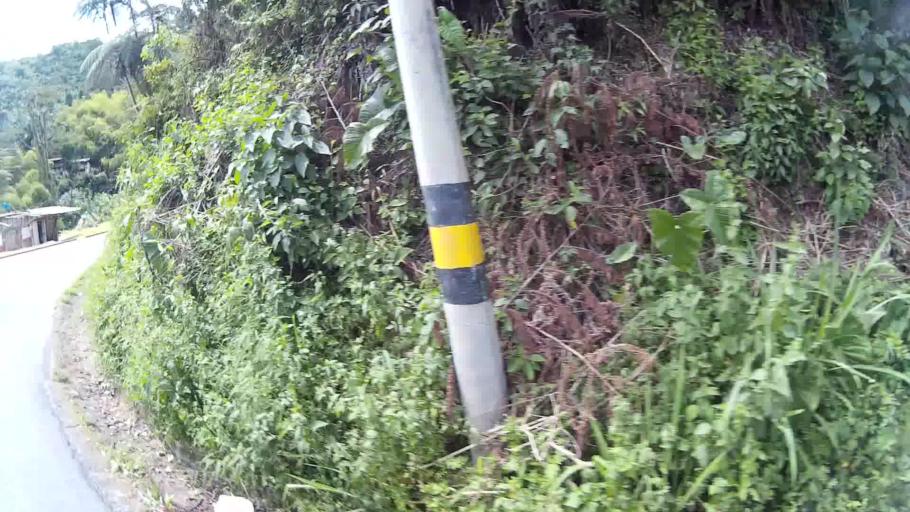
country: CO
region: Risaralda
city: Marsella
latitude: 4.9024
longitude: -75.7317
